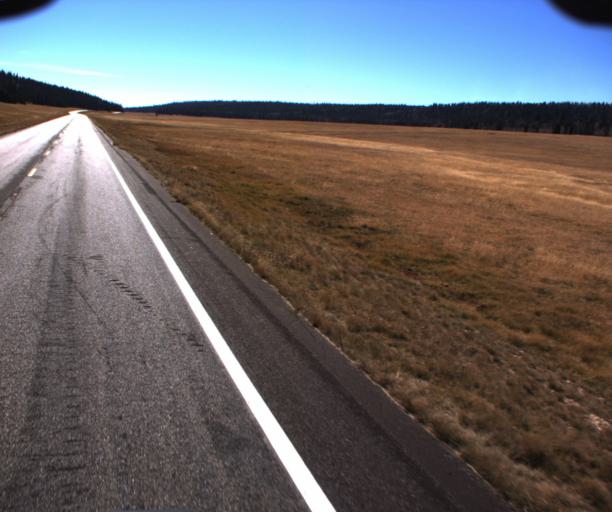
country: US
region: Arizona
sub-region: Coconino County
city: Grand Canyon
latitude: 36.3957
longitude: -112.1283
